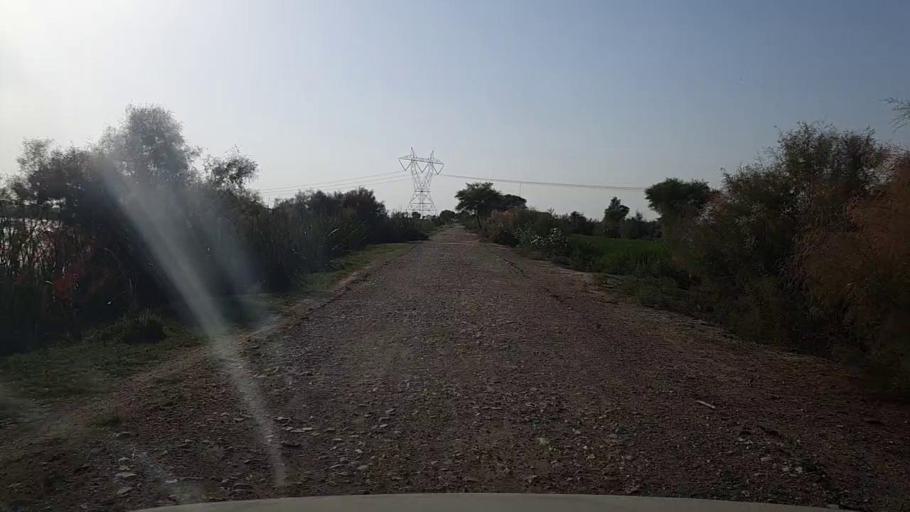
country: PK
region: Sindh
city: Kandhkot
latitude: 28.2911
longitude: 69.3230
